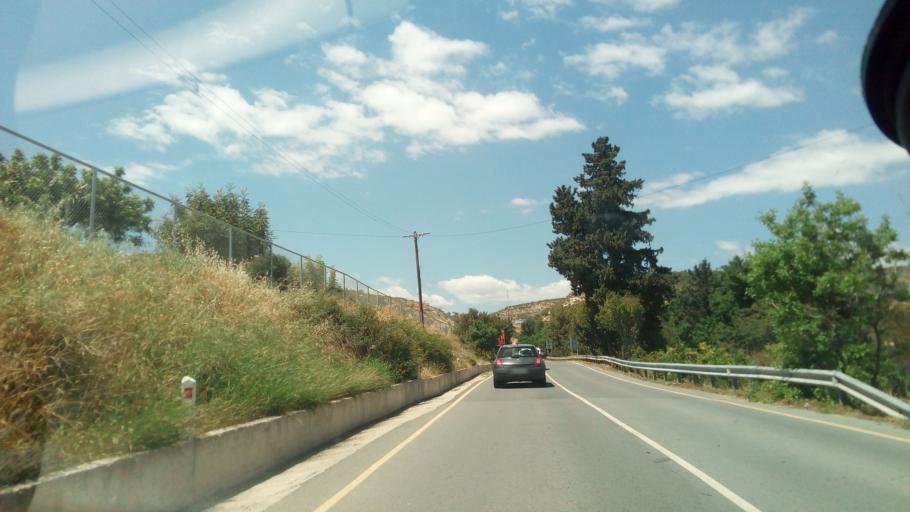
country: CY
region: Limassol
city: Erimi
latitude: 34.6942
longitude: 32.9064
